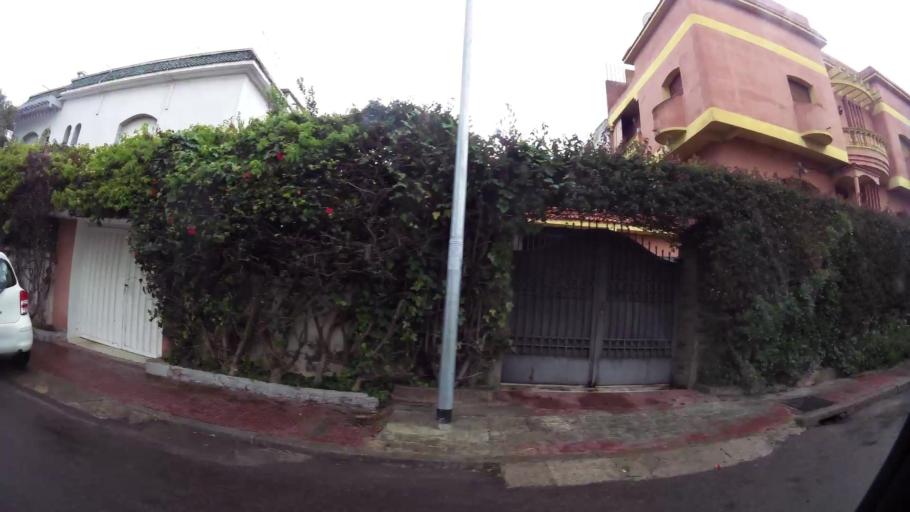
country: MA
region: Grand Casablanca
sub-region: Casablanca
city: Casablanca
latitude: 33.5581
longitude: -7.6814
